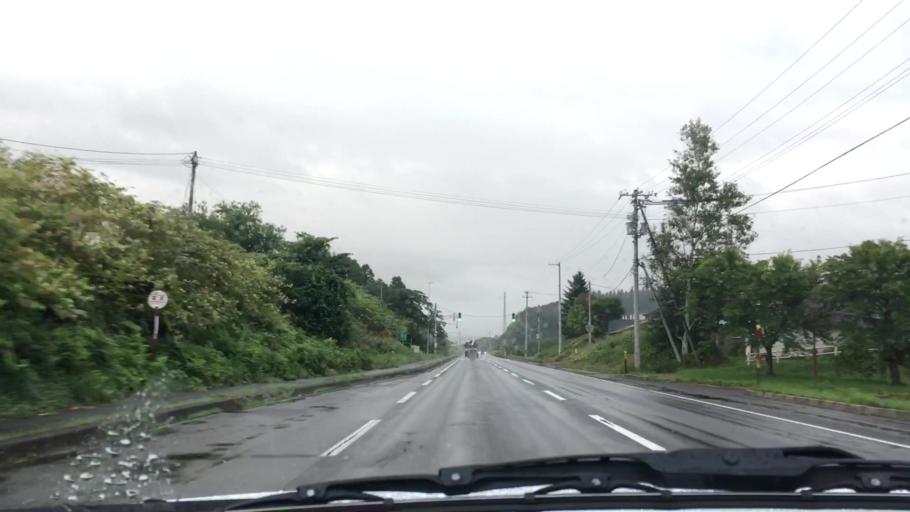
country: JP
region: Hokkaido
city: Nanae
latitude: 42.1749
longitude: 140.4534
